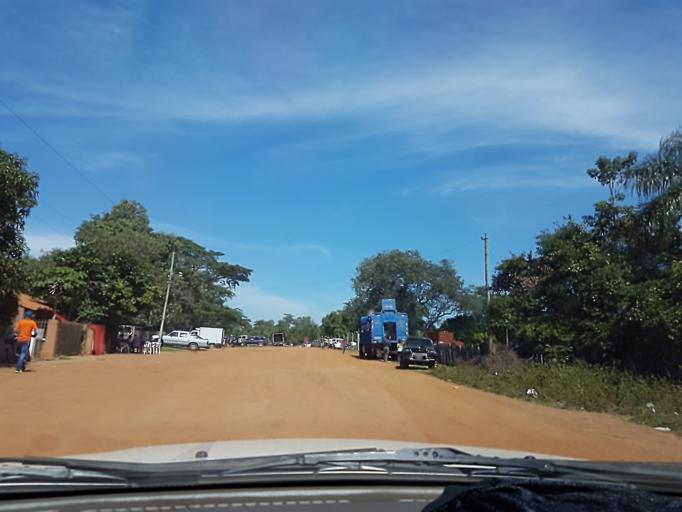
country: PY
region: Cordillera
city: Arroyos y Esteros
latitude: -24.9951
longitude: -57.2153
